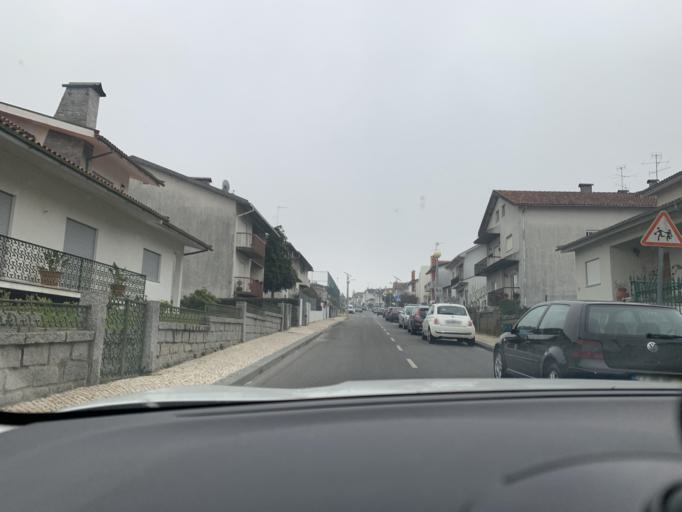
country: PT
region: Viseu
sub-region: Viseu
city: Rio de Loba
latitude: 40.6620
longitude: -7.8922
